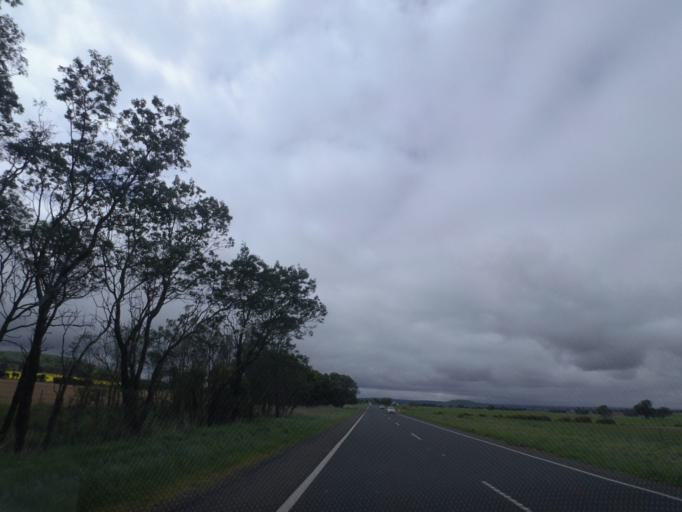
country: AU
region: Victoria
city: Brown Hill
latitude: -37.4097
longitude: 143.9485
